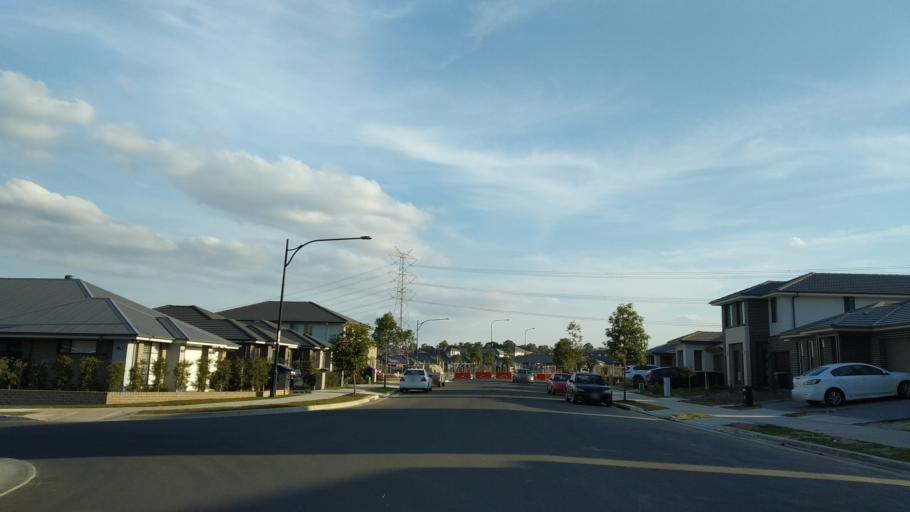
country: AU
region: New South Wales
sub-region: Penrith Municipality
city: Werrington County
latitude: -33.7365
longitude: 150.7527
